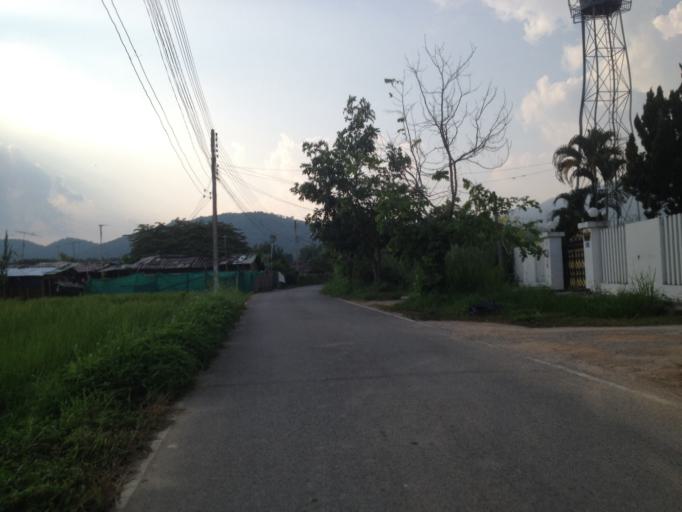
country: TH
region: Chiang Mai
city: Hang Dong
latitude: 18.7480
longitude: 98.9313
